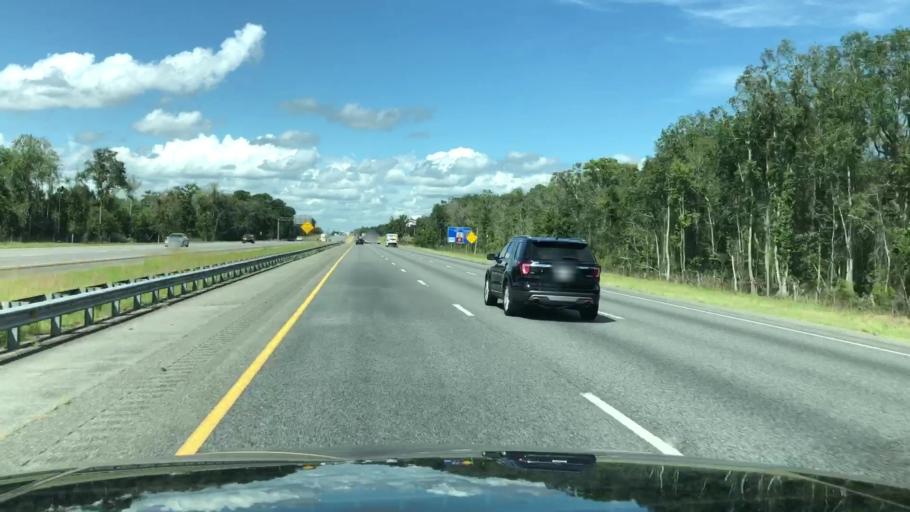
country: US
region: Georgia
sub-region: Lowndes County
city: Valdosta
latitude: 30.7927
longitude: -83.3022
